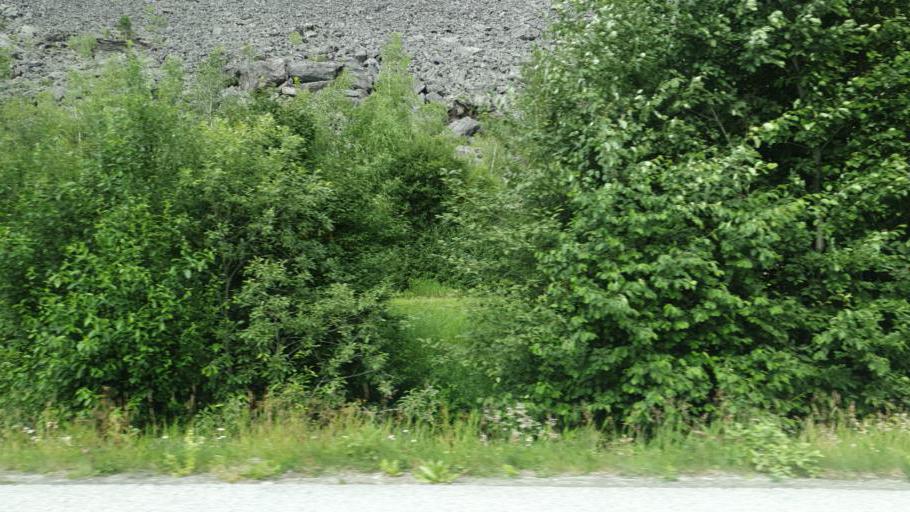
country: NO
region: Oppland
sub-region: Sel
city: Otta
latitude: 61.8421
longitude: 9.3971
